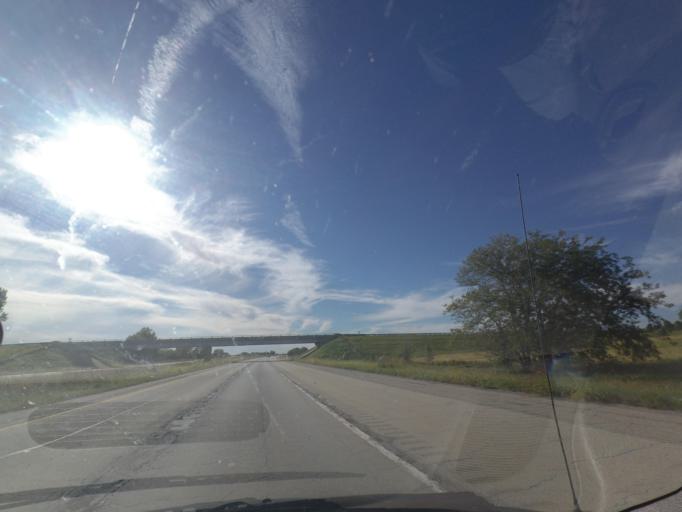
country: US
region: Illinois
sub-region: Macon County
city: Forsyth
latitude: 39.9078
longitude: -88.9724
